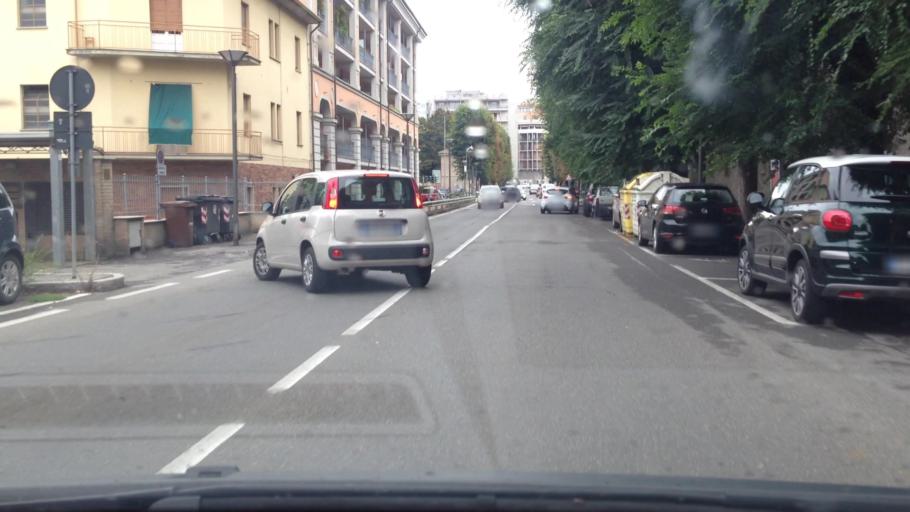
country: IT
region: Piedmont
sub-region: Provincia di Alessandria
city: Tortona
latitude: 44.8964
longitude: 8.8589
